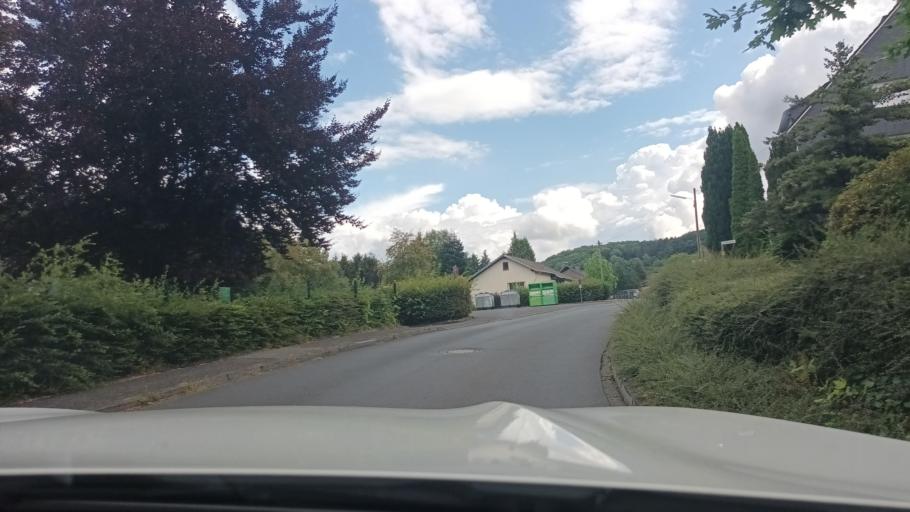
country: DE
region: Rheinland-Pfalz
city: Kircheib
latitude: 50.7345
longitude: 7.4525
